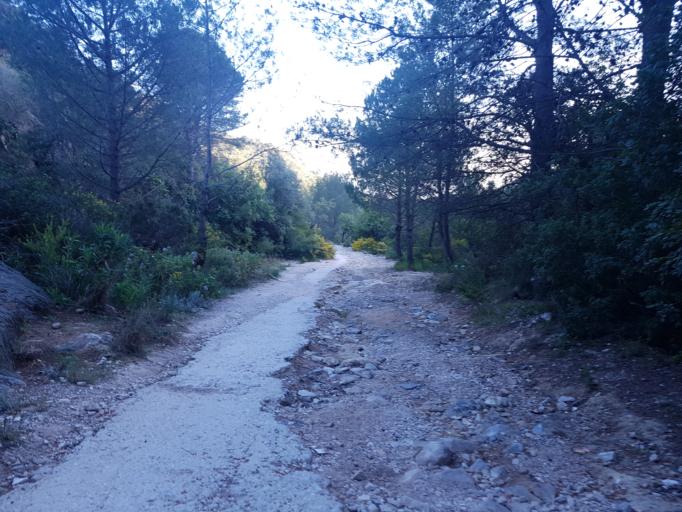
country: ES
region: Andalusia
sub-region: Provincia de Malaga
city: Marbella
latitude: 36.5399
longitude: -4.8845
